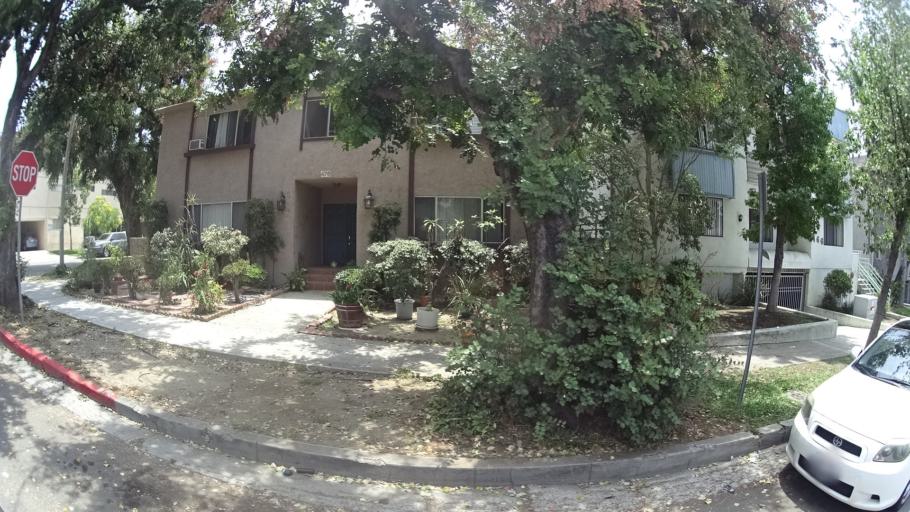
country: US
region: California
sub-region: Los Angeles County
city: Burbank
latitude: 34.1856
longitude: -118.3072
